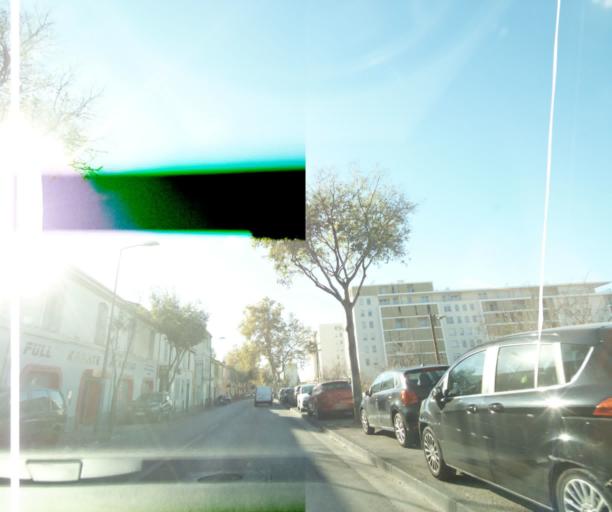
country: FR
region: Provence-Alpes-Cote d'Azur
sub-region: Departement des Bouches-du-Rhone
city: Marseille 11
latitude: 43.2844
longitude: 5.4366
